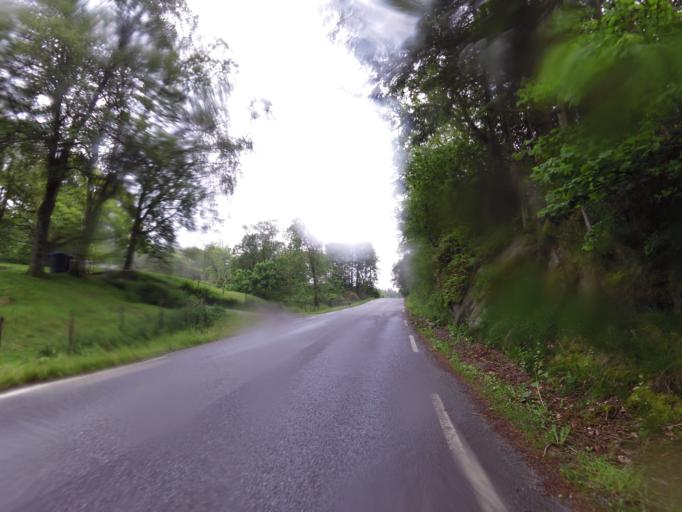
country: NO
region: Hordaland
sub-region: Sveio
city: Sveio
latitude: 59.5265
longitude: 5.2802
